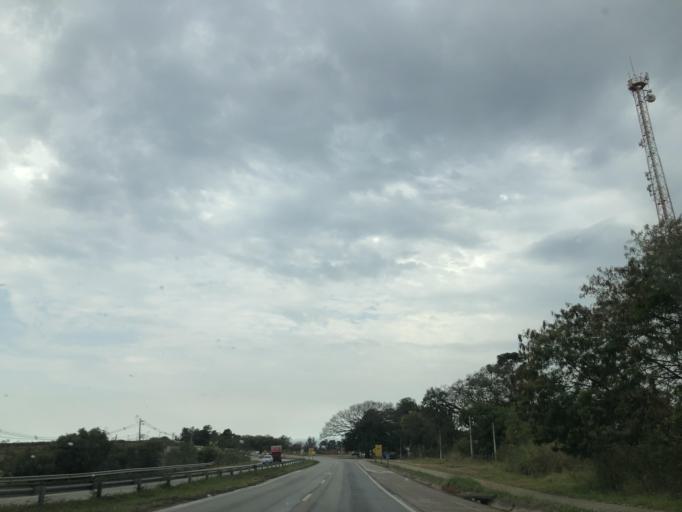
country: BR
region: Sao Paulo
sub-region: Votorantim
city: Votorantim
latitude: -23.5767
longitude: -47.5164
